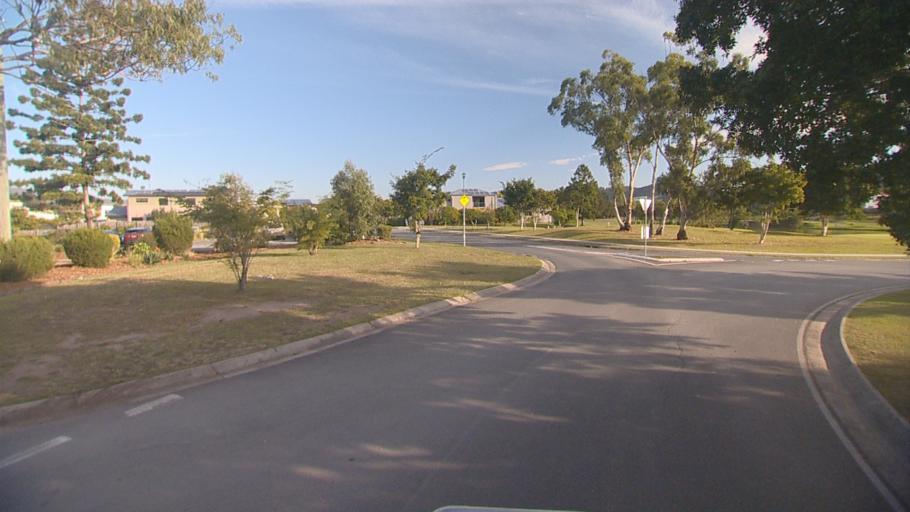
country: AU
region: Queensland
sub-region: Logan
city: Windaroo
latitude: -27.7425
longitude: 153.1974
